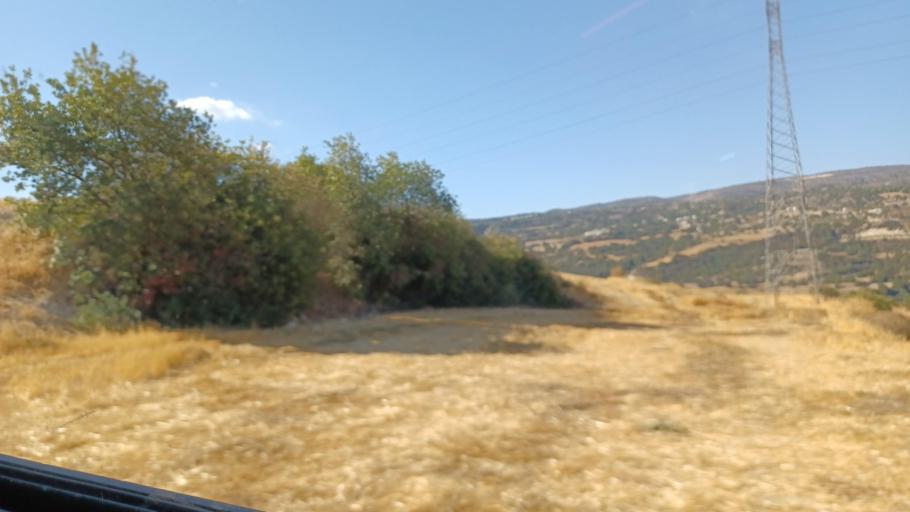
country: CY
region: Pafos
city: Polis
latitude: 34.9649
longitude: 32.4659
